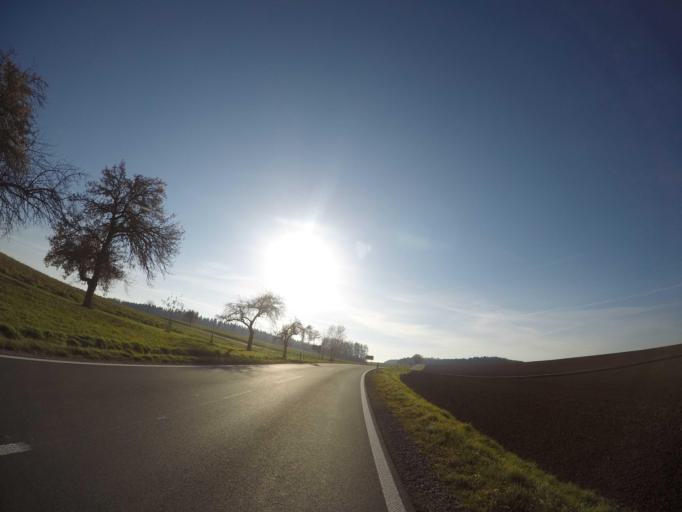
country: DE
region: Baden-Wuerttemberg
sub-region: Tuebingen Region
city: Oberstadion
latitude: 48.1895
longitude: 9.6622
